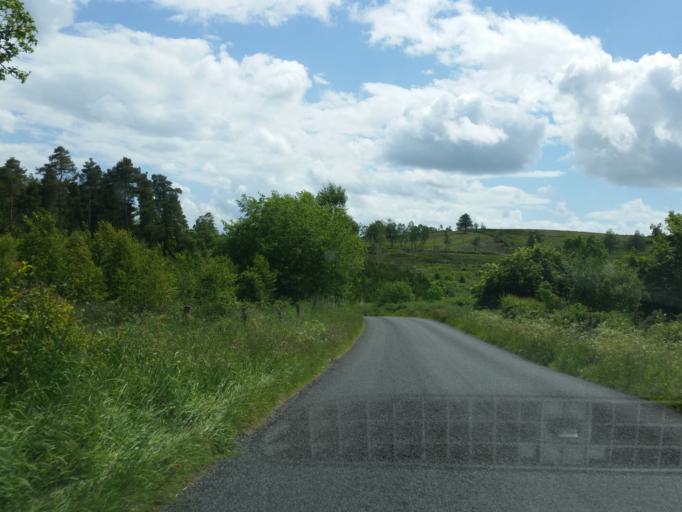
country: GB
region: Northern Ireland
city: Fivemiletown
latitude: 54.3564
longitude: -7.3039
